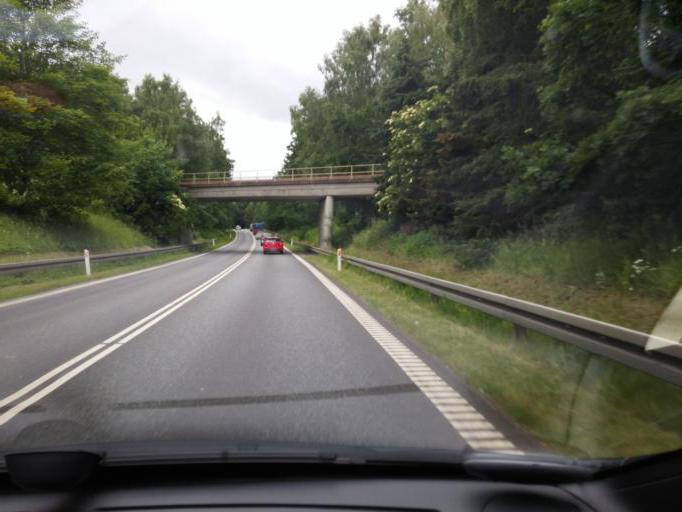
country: DK
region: Capital Region
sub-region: Hillerod Kommune
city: Nodebo
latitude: 55.9468
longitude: 12.3424
